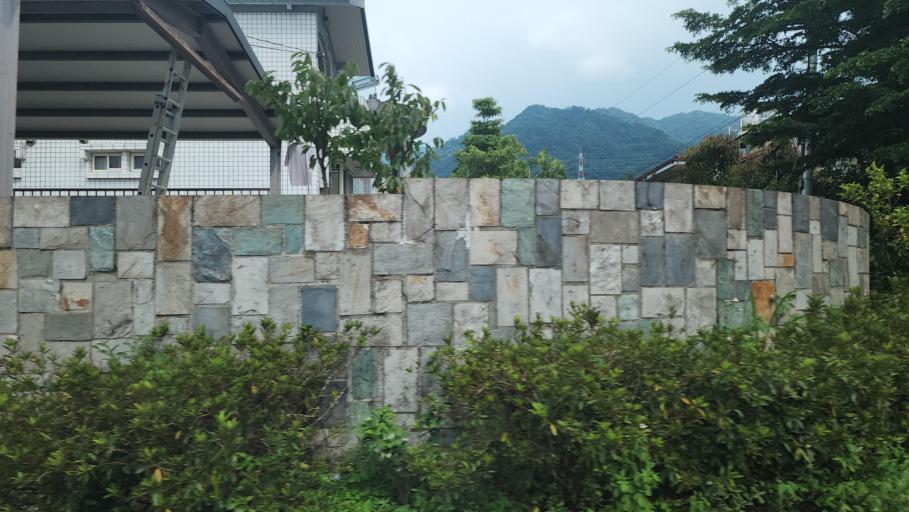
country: TW
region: Taiwan
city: Daxi
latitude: 24.9085
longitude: 121.3900
